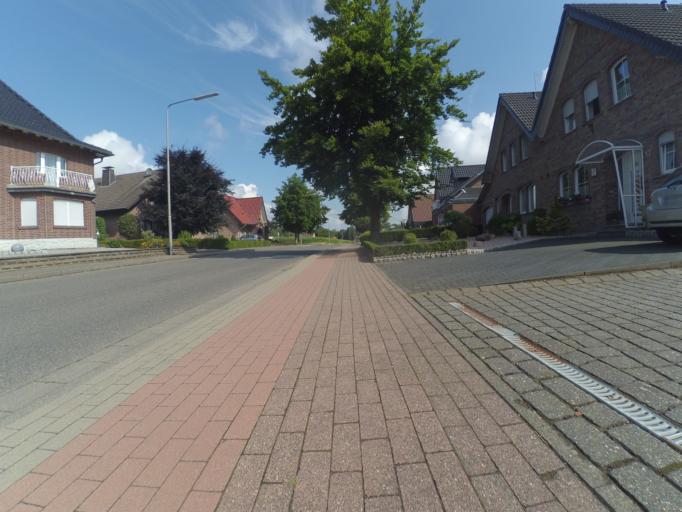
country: NL
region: Limburg
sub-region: Gemeente Echt-Susteren
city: Koningsbosch
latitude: 51.0300
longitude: 5.9608
